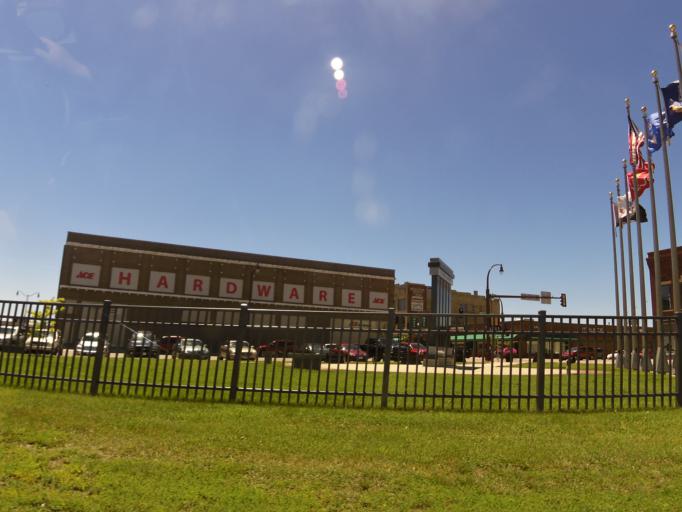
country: US
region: Minnesota
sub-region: Becker County
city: Detroit Lakes
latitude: 46.8190
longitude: -95.8449
